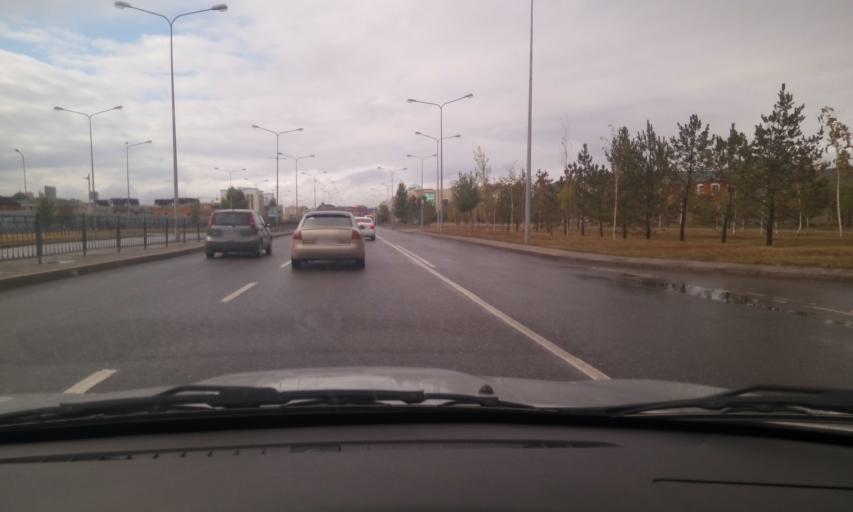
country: KZ
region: Astana Qalasy
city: Astana
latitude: 51.1468
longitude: 71.4008
